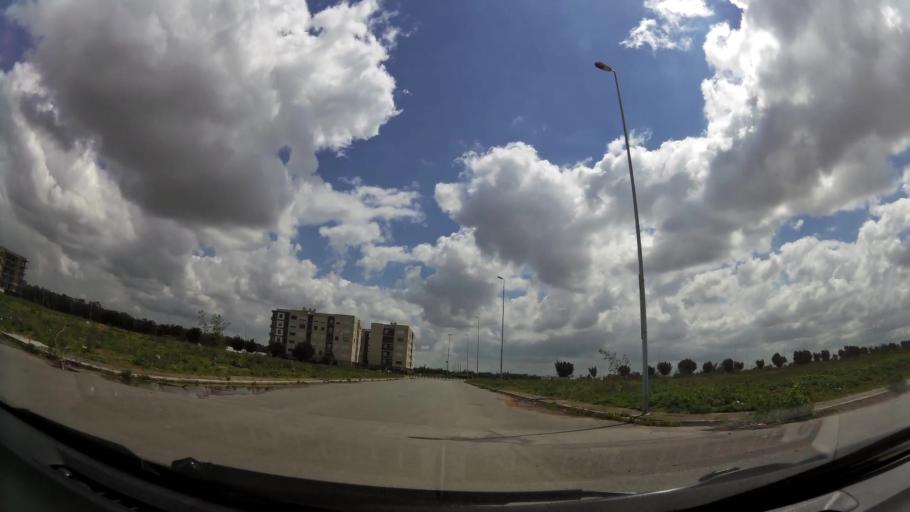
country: MA
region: Chaouia-Ouardigha
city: Nouaseur
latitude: 33.3872
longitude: -7.5599
